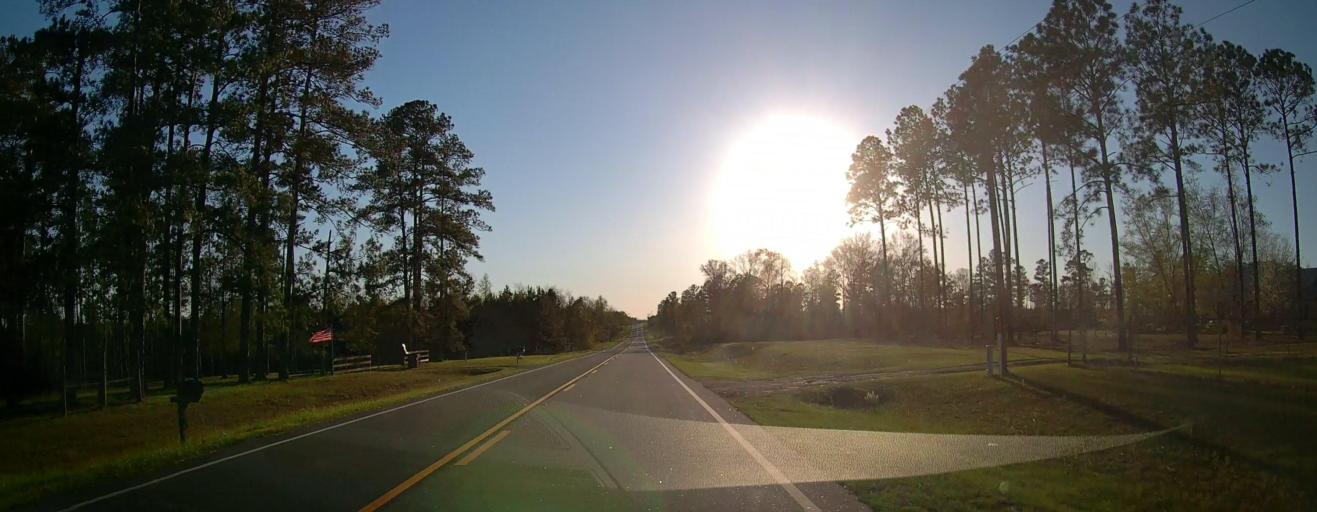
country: US
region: Georgia
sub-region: Wilcox County
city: Abbeville
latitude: 31.9694
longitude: -83.3771
